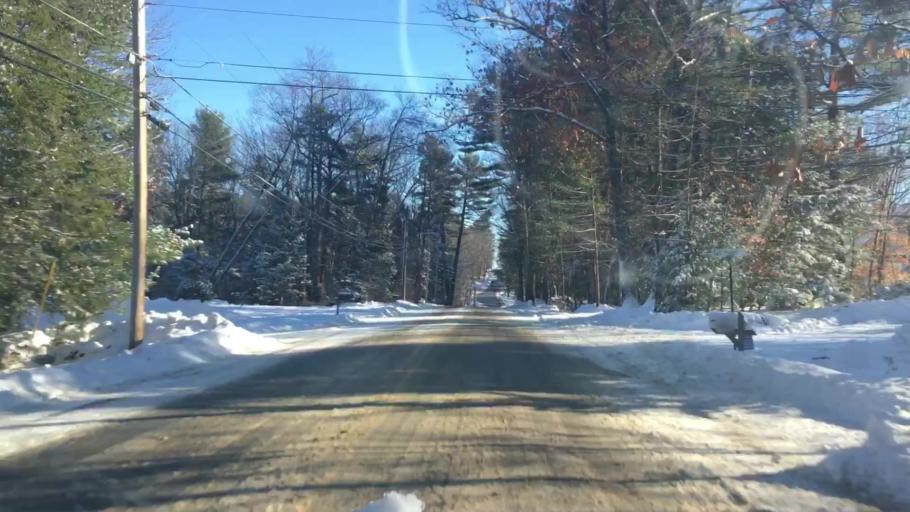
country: US
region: Maine
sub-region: Cumberland County
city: New Gloucester
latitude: 43.9508
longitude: -70.3069
